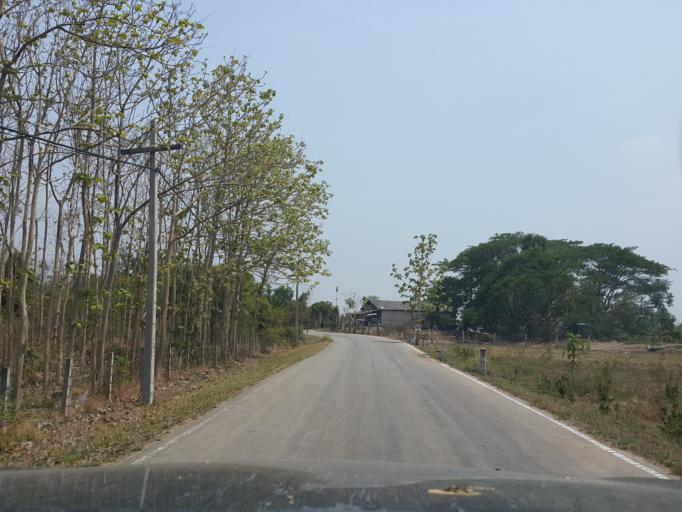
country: TH
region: Lampang
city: Mae Phrik
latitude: 17.5288
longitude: 99.1481
